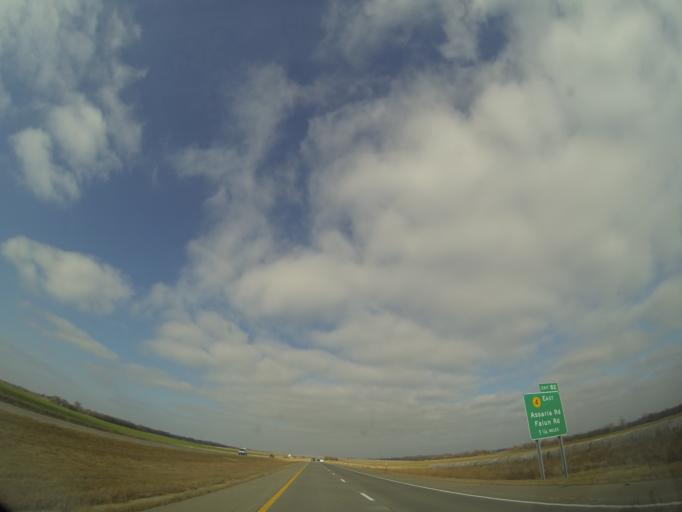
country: US
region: Kansas
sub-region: McPherson County
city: Lindsborg
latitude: 38.6612
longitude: -97.6215
